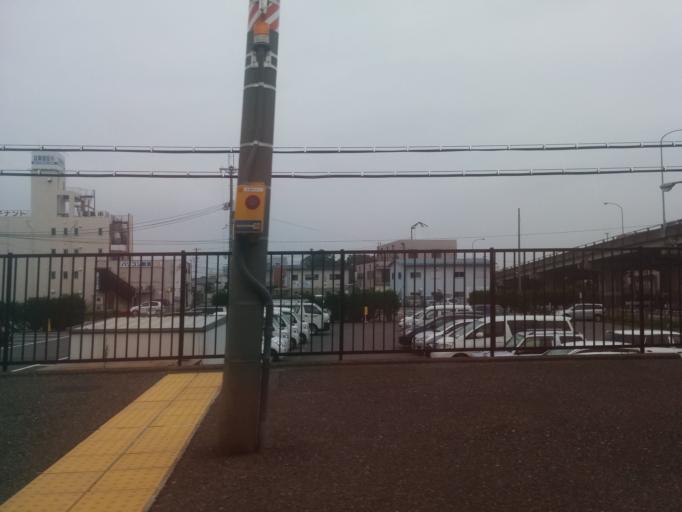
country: JP
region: Shiga Prefecture
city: Hikone
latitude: 35.2468
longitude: 136.2488
